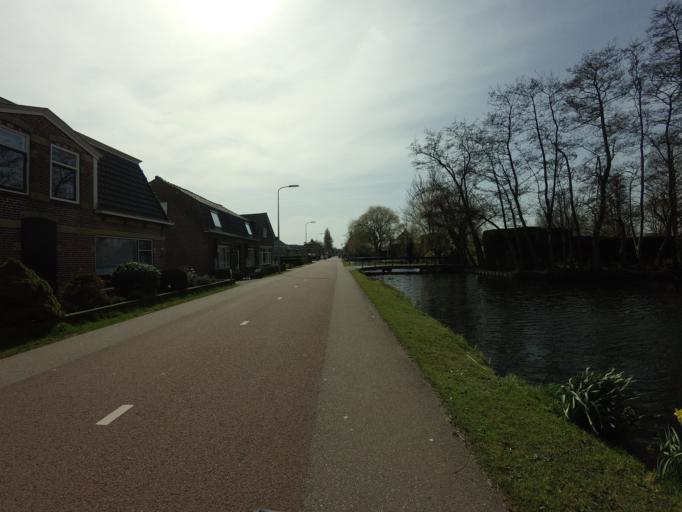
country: NL
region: South Holland
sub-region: Gemeente Den Haag
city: Ypenburg
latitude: 52.0623
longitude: 4.4018
